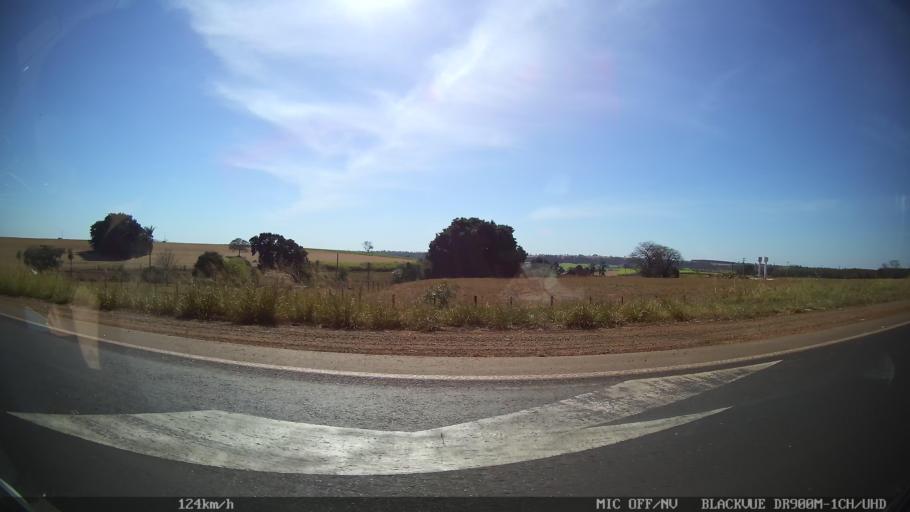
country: BR
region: Sao Paulo
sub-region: Olimpia
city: Olimpia
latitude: -20.6230
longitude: -48.7729
